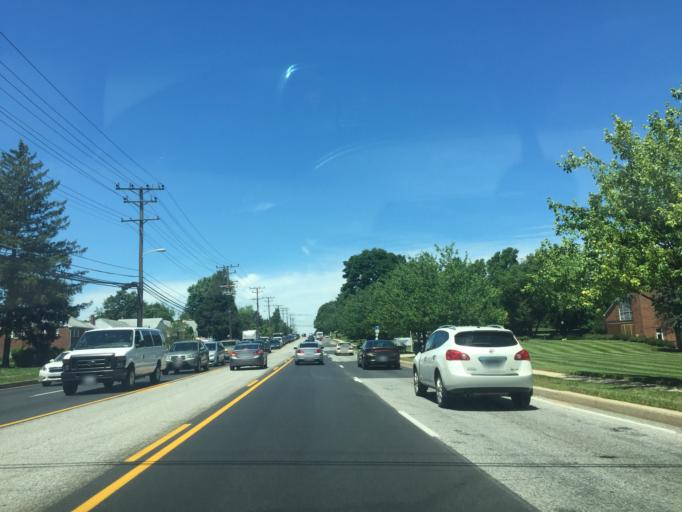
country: US
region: Maryland
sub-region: Baltimore County
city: Milford Mill
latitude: 39.3571
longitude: -76.7675
